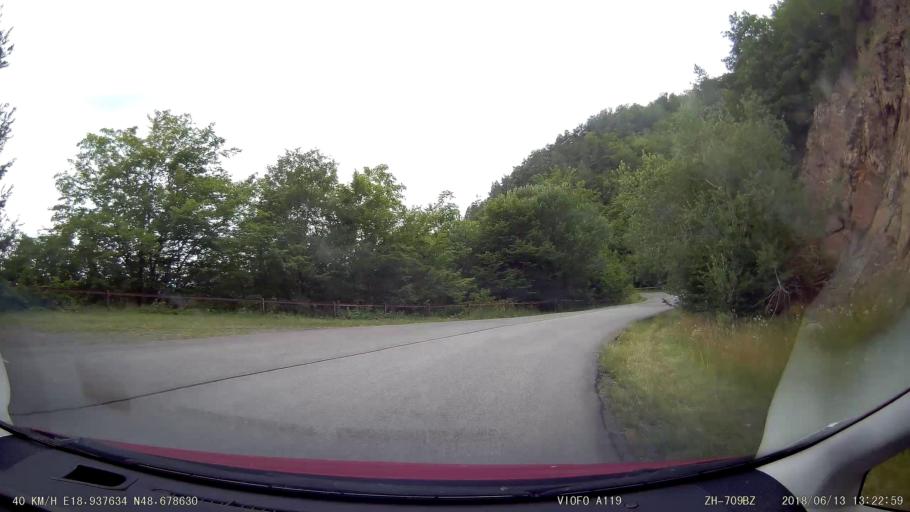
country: SK
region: Banskobystricky
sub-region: Okres Ziar nad Hronom
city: Kremnica
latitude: 48.6786
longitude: 18.9374
